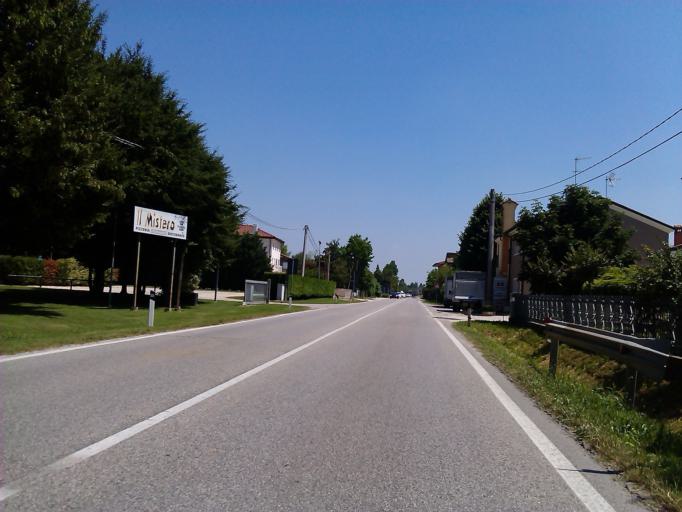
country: IT
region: Veneto
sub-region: Provincia di Padova
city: Massanzago-Ca' Baglioni-San Dono
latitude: 45.5555
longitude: 11.9751
